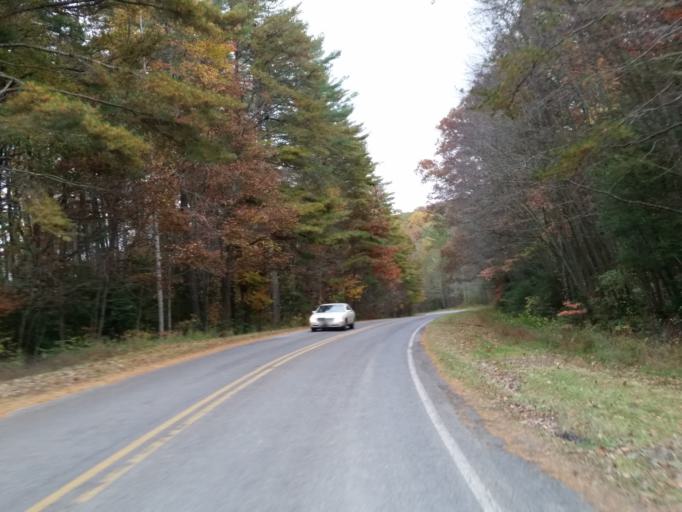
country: US
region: Georgia
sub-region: Fannin County
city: Blue Ridge
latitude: 34.6907
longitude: -84.2567
